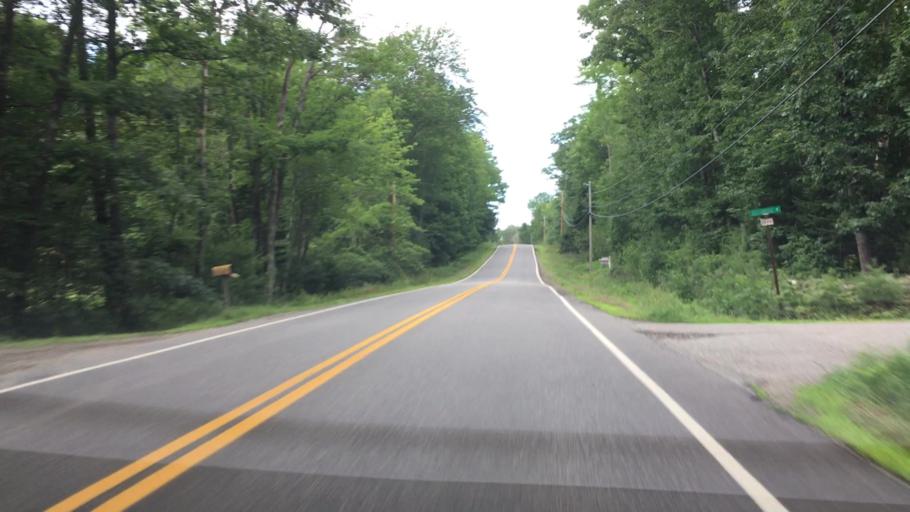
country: US
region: Maine
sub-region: Waldo County
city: Lincolnville
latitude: 44.3339
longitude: -69.0577
